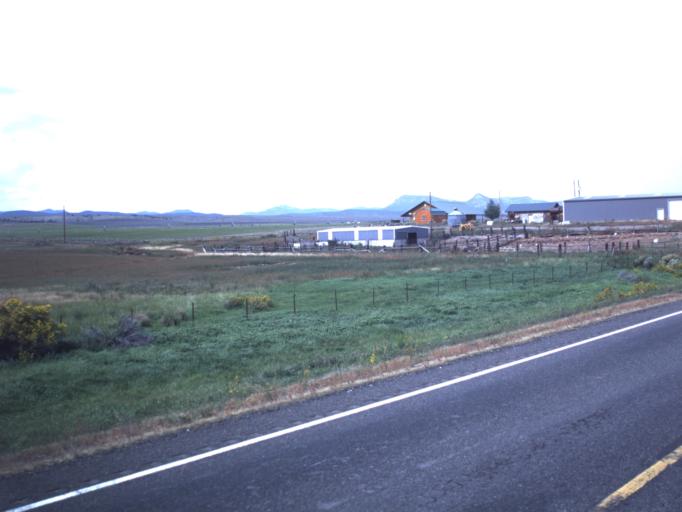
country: US
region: Utah
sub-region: Garfield County
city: Panguitch
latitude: 37.8999
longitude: -112.4321
